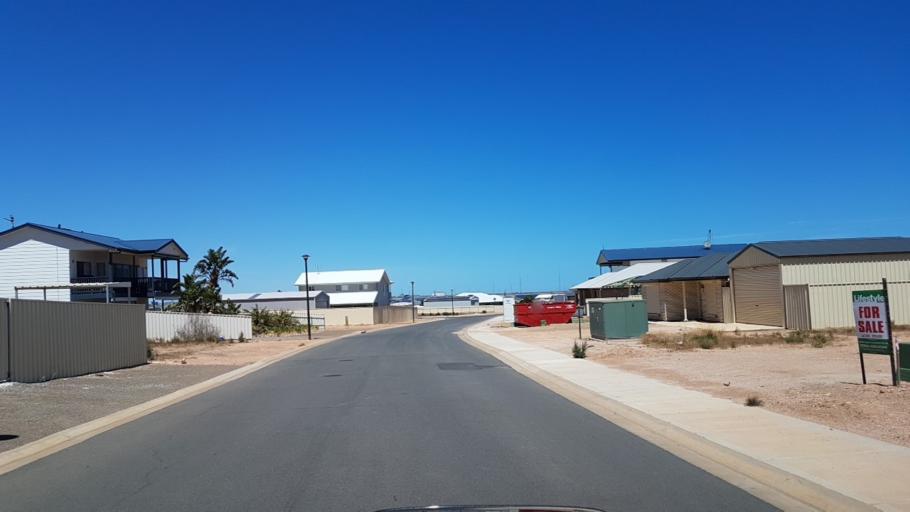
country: AU
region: South Australia
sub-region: Copper Coast
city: Wallaroo
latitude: -33.8920
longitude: 137.6307
